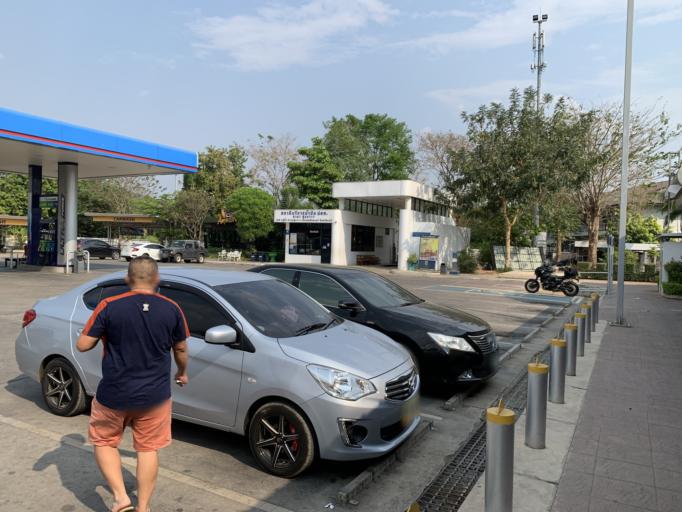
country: TH
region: Phrae
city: Phrae
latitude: 18.1548
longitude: 100.1602
